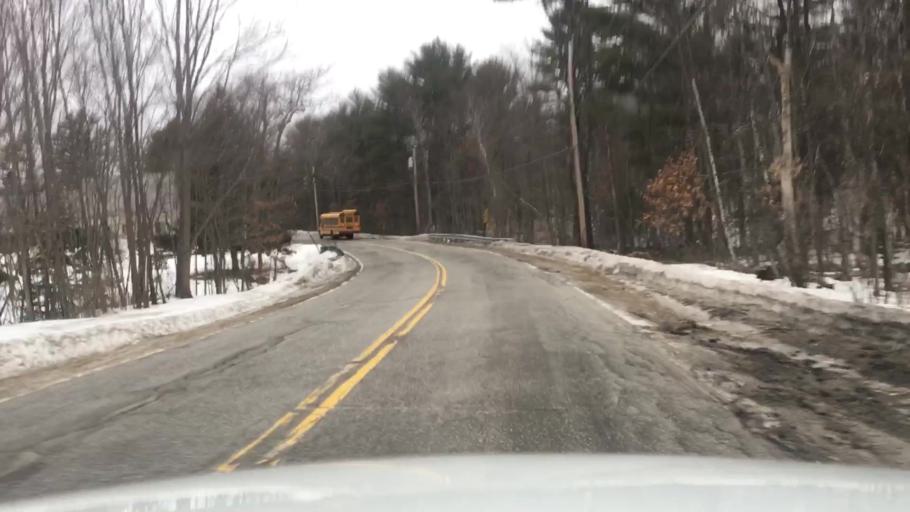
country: US
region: Maine
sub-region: York County
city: Shapleigh
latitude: 43.5424
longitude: -70.8492
